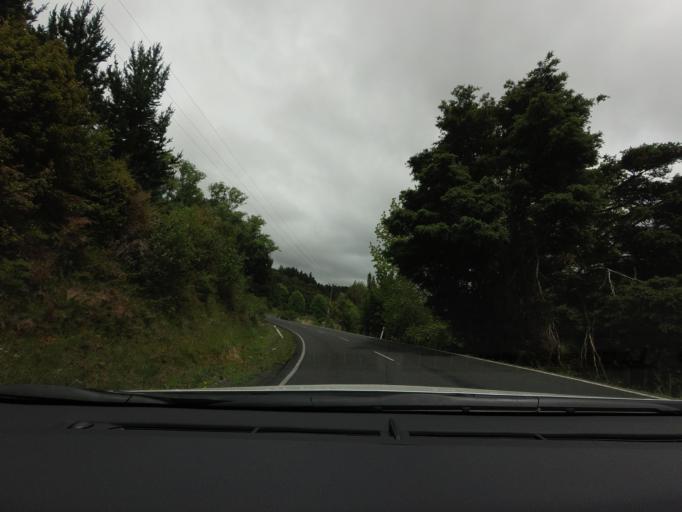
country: NZ
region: Auckland
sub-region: Auckland
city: Warkworth
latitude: -36.5030
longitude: 174.6411
